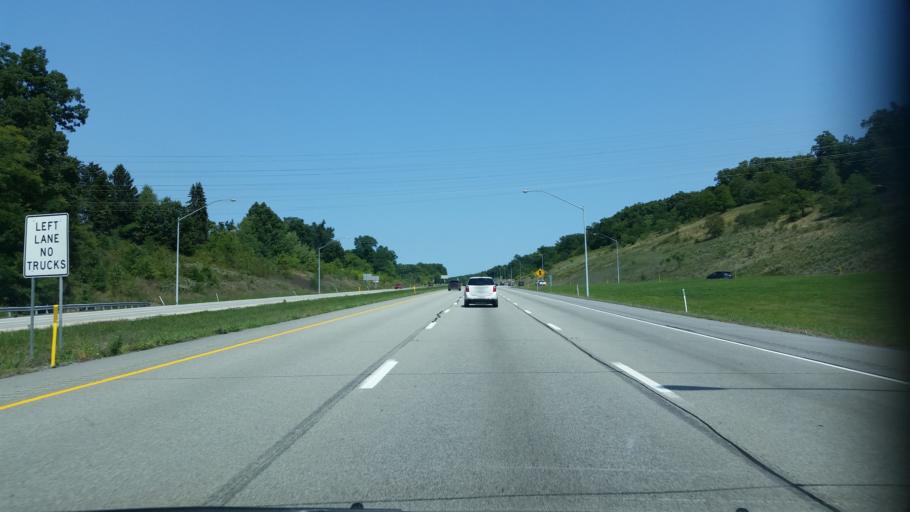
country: US
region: Pennsylvania
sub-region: Blair County
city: Lakemont
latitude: 40.4959
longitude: -78.3810
